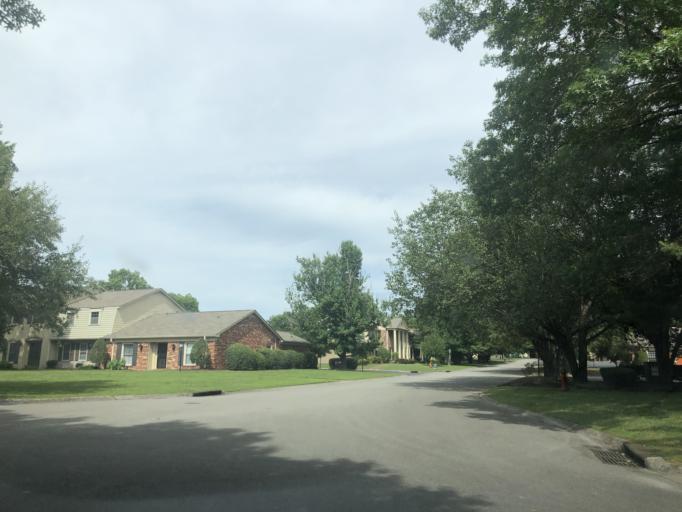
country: US
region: Tennessee
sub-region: Davidson County
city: Belle Meade
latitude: 36.0738
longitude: -86.9488
